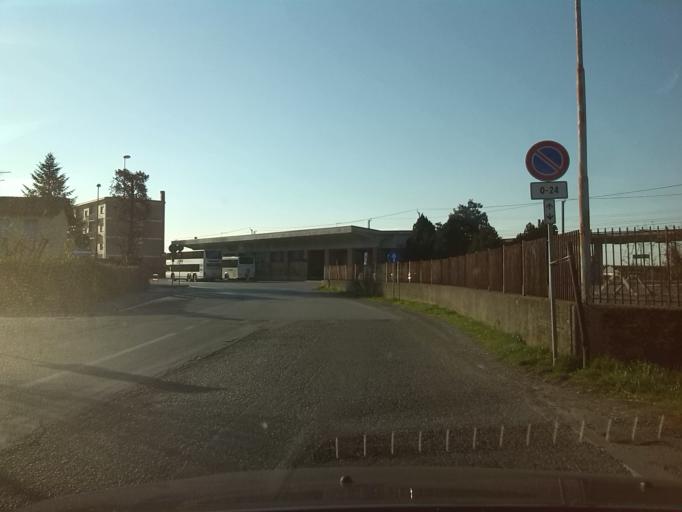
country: IT
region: Friuli Venezia Giulia
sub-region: Provincia di Gorizia
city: Cormons
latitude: 45.9584
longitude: 13.4613
